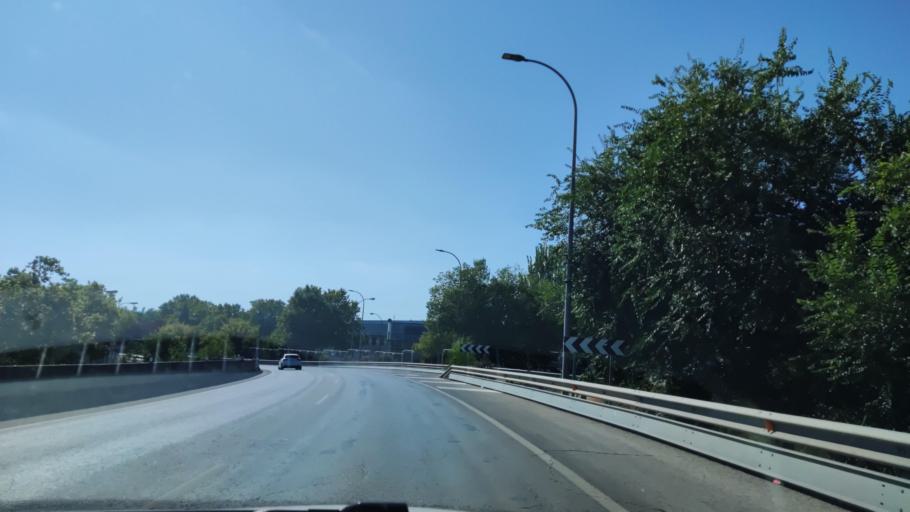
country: ES
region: Madrid
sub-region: Provincia de Madrid
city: Alcorcon
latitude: 40.3588
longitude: -3.8077
